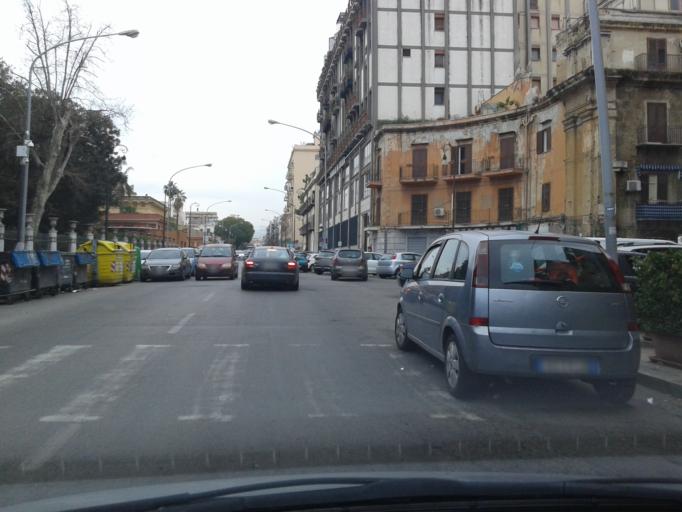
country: IT
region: Sicily
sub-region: Palermo
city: Palermo
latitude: 38.1144
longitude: 13.3746
